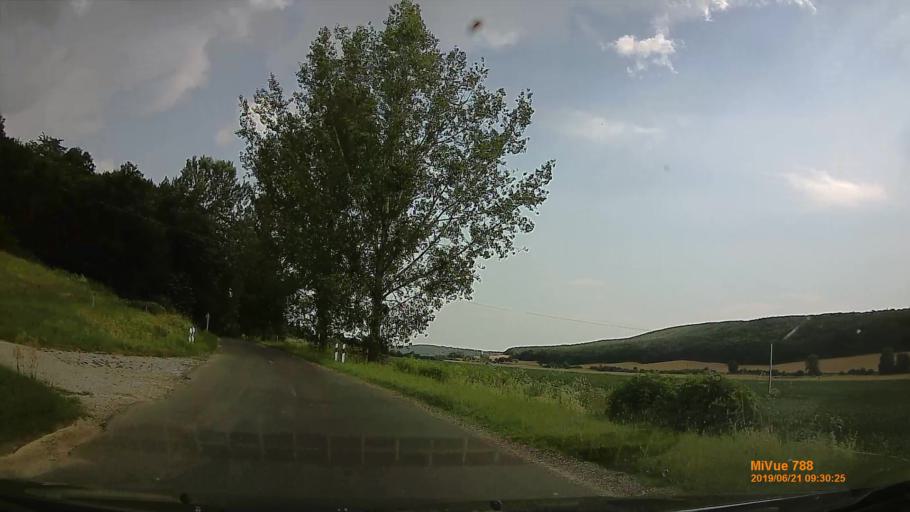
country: HU
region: Somogy
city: Taszar
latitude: 46.2961
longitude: 17.8815
